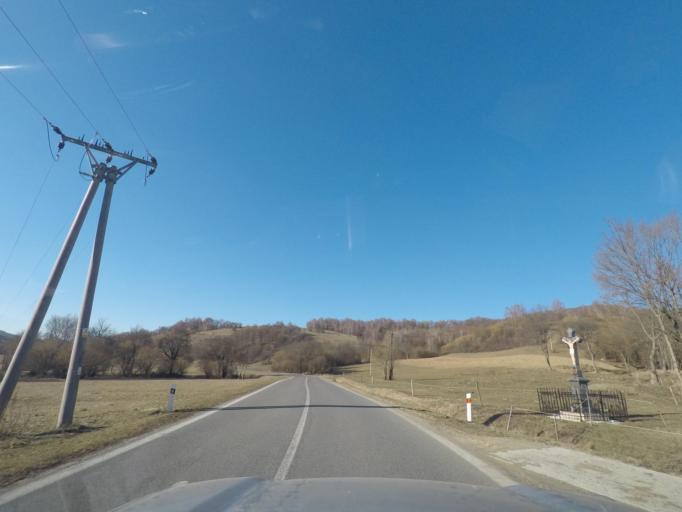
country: SK
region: Presovsky
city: Medzilaborce
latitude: 49.1765
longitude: 22.0241
